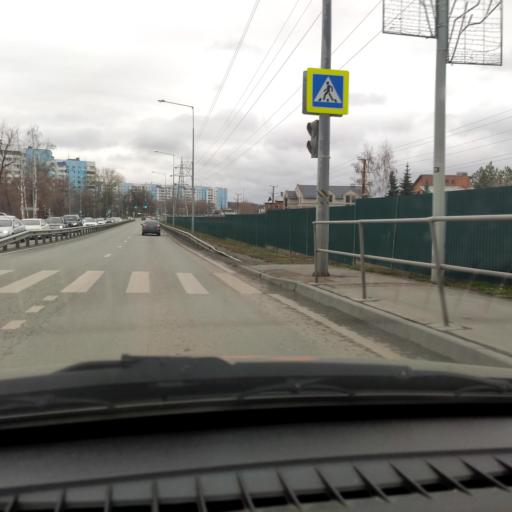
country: RU
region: Samara
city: Volzhskiy
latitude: 53.3512
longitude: 50.2199
